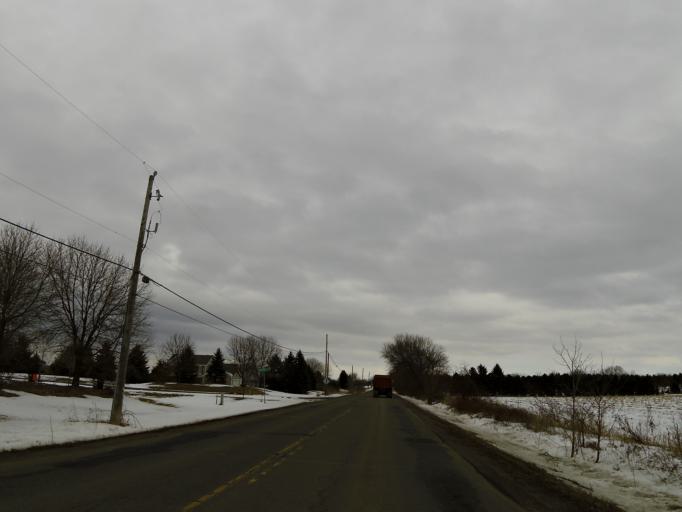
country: US
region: Wisconsin
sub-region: Saint Croix County
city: Hudson
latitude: 44.9802
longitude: -92.7896
